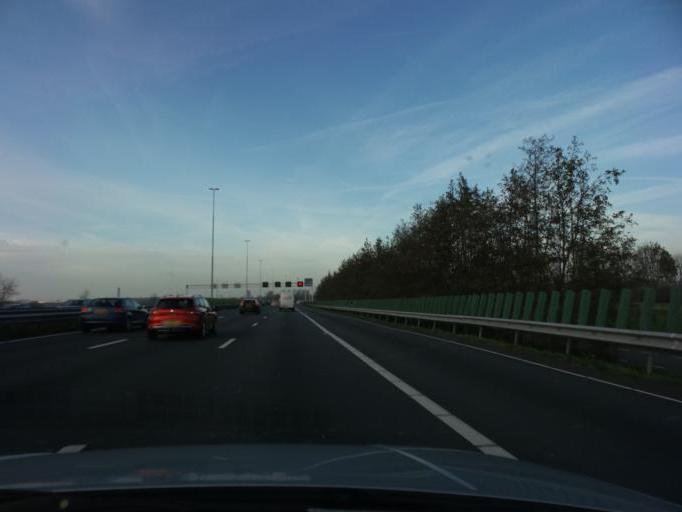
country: NL
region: South Holland
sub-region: Gemeente Schiedam
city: Schiedam
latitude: 51.9692
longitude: 4.4015
